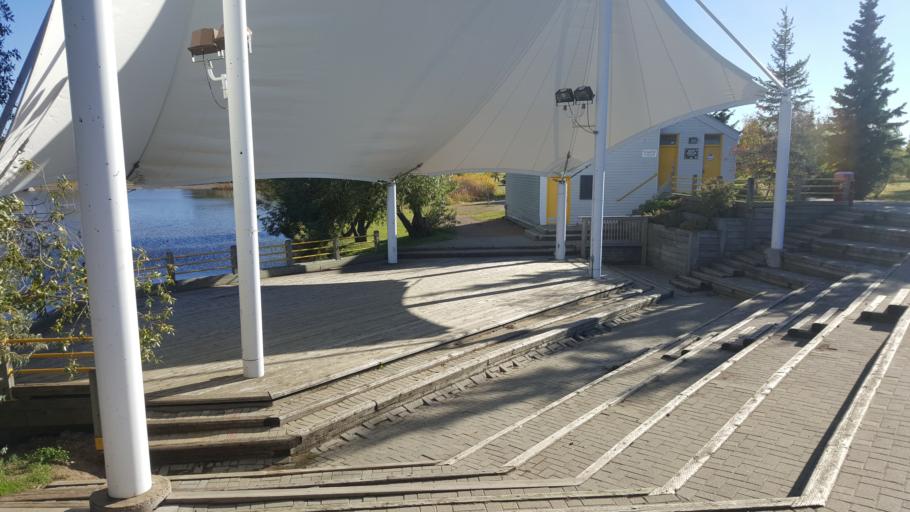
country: CA
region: Saskatchewan
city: Lloydminster
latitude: 53.2593
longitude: -110.0423
